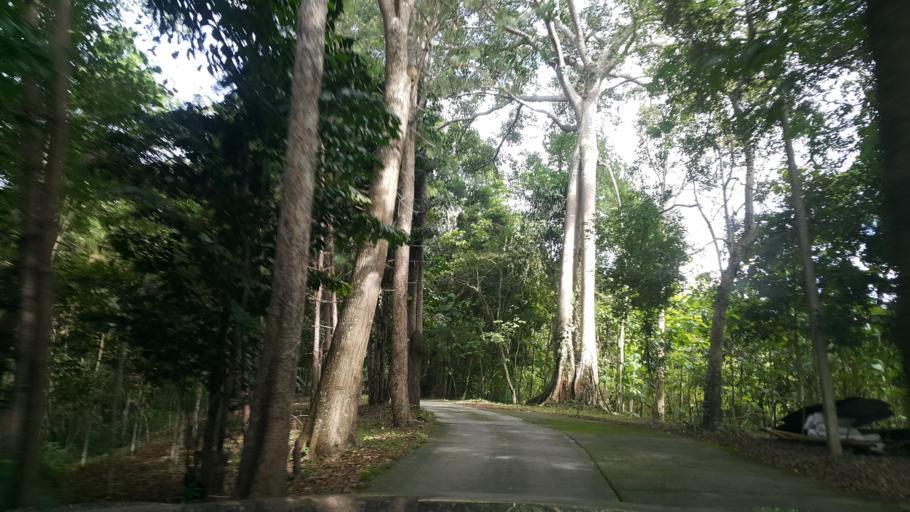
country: TH
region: Loei
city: Na Haeo
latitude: 17.5596
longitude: 100.9531
